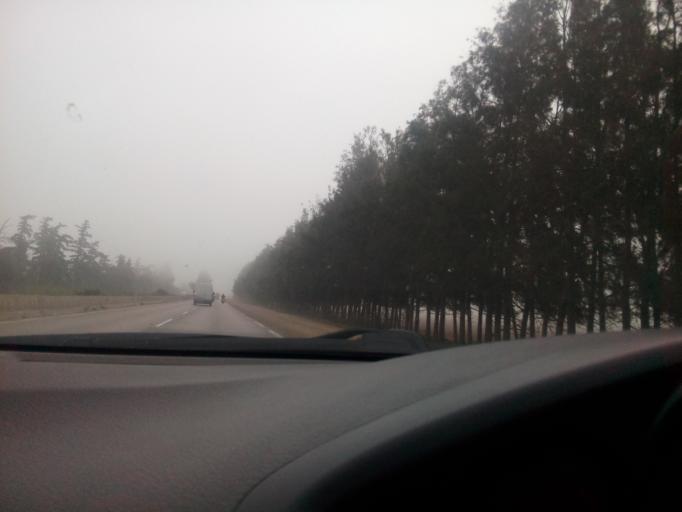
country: DZ
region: Oran
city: Bou Tlelis
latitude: 35.5818
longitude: -0.8282
